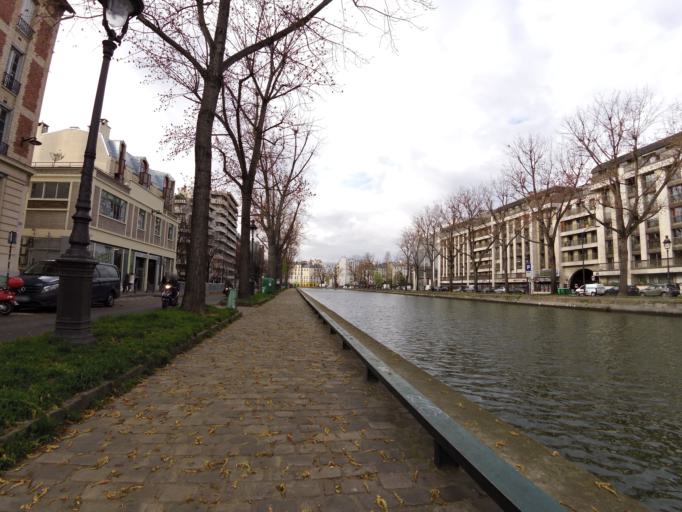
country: FR
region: Ile-de-France
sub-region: Paris
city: Paris
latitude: 48.8762
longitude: 2.3647
